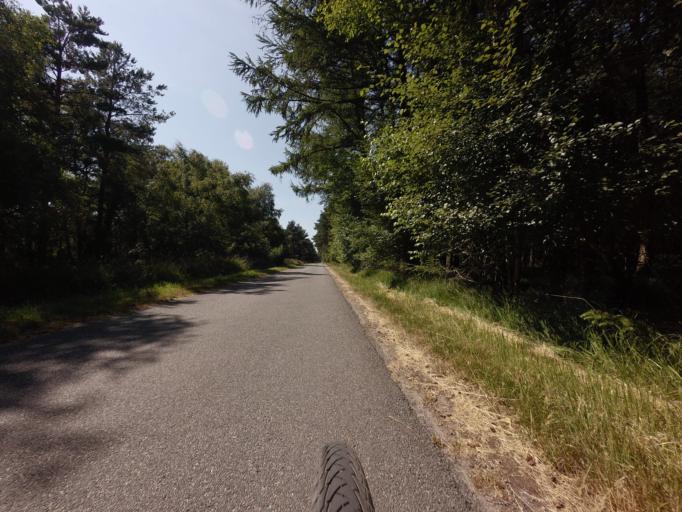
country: DK
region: North Denmark
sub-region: Laeso Kommune
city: Byrum
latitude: 57.2905
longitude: 10.9630
